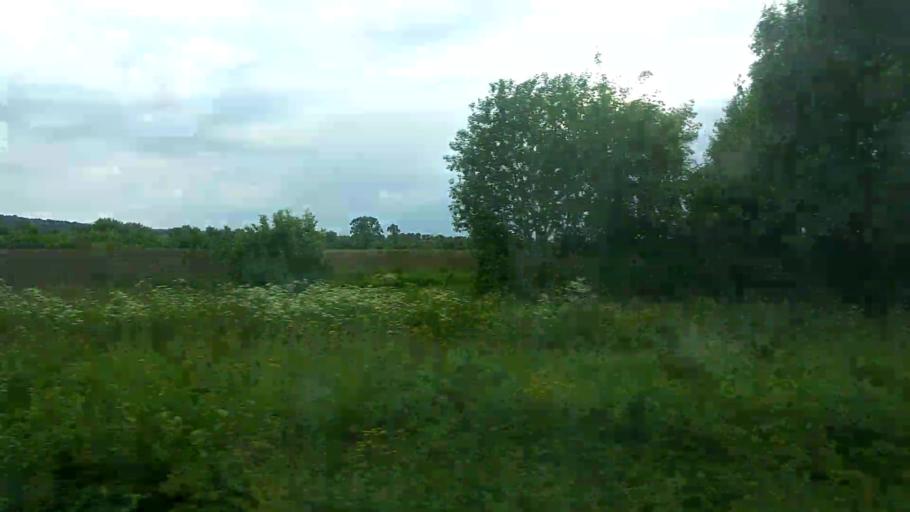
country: RU
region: Moskovskaya
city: Ozery
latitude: 54.8385
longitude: 38.5795
